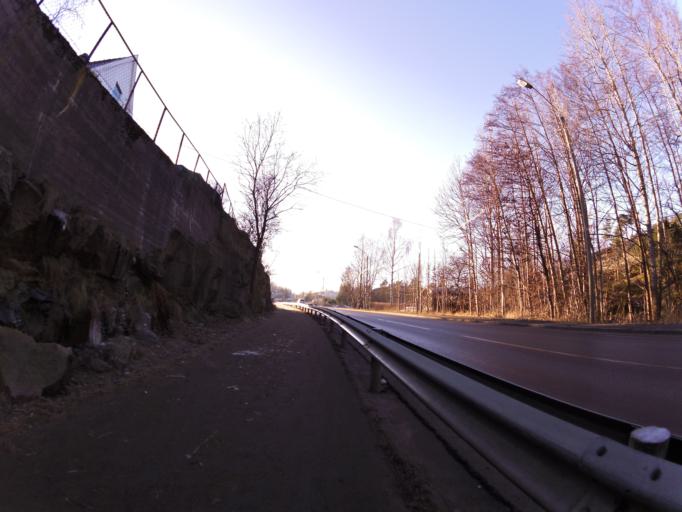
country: NO
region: Ostfold
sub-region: Fredrikstad
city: Fredrikstad
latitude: 59.2026
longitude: 10.8777
